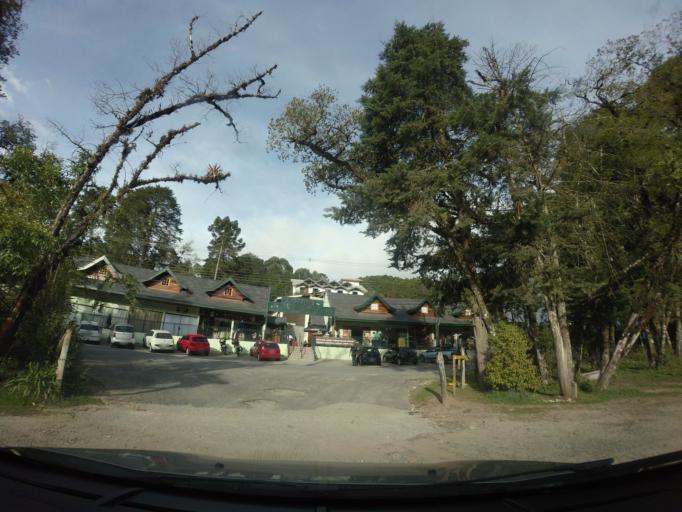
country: BR
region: Sao Paulo
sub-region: Campos Do Jordao
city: Campos do Jordao
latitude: -22.7385
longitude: -45.5689
